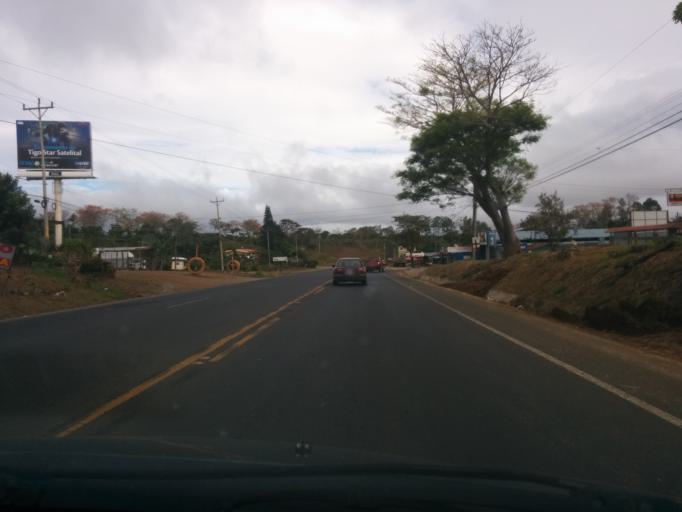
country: CR
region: Alajuela
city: San Rafael
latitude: 10.0706
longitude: -84.4558
